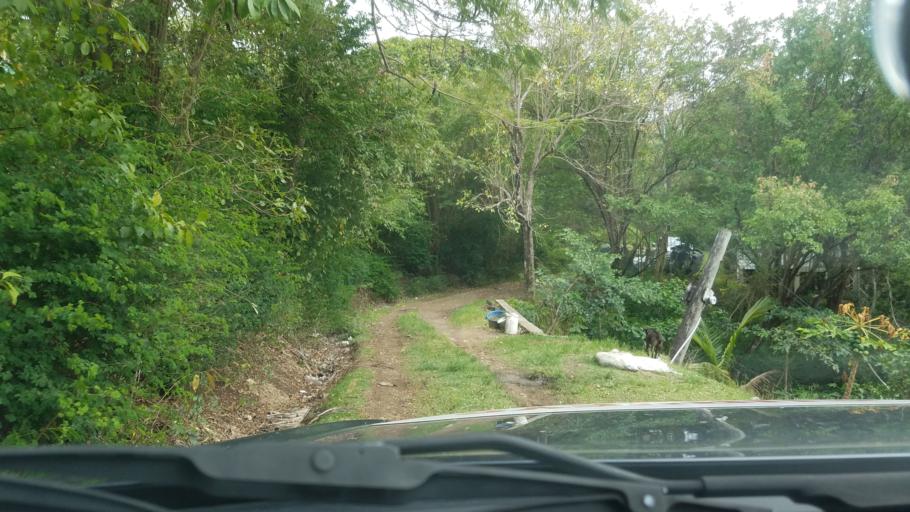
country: LC
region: Gros-Islet
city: Gros Islet
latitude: 14.0636
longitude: -60.9533
